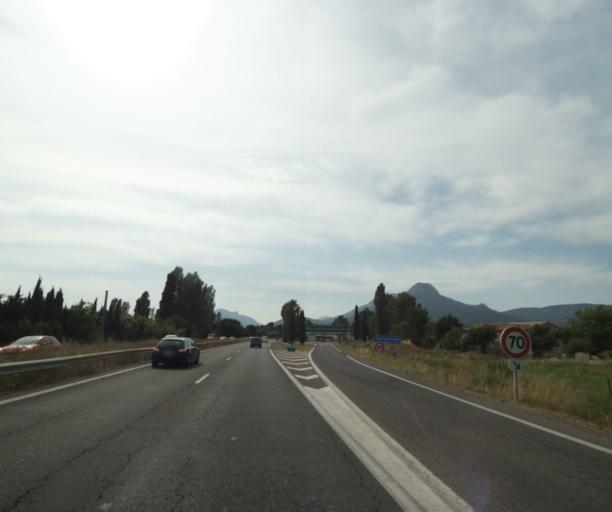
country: FR
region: Provence-Alpes-Cote d'Azur
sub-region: Departement du Var
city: La Crau
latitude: 43.1338
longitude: 6.0504
